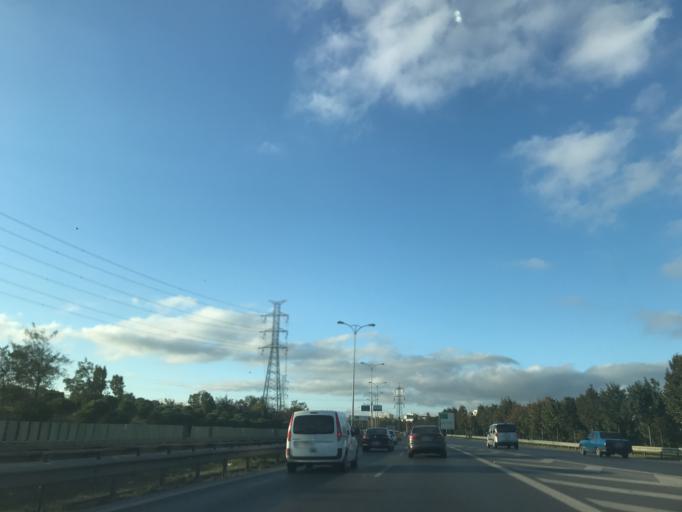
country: TR
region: Istanbul
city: Esenler
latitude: 41.0602
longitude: 28.8857
